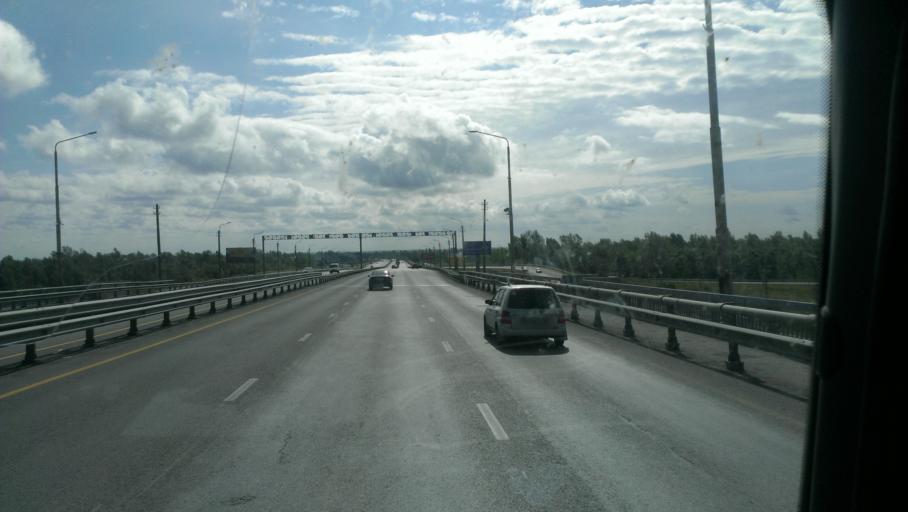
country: RU
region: Altai Krai
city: Zaton
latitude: 53.3210
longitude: 83.8103
